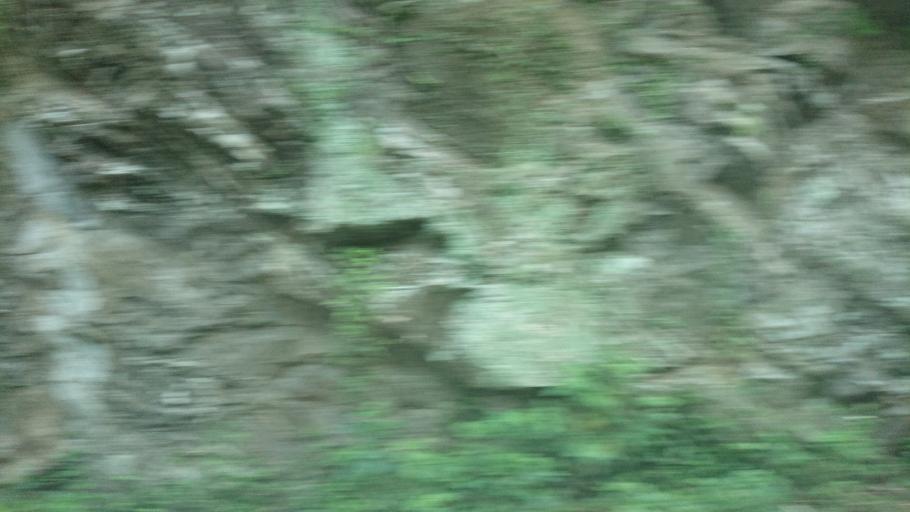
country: TW
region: Taiwan
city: Daxi
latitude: 24.8817
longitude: 121.3799
